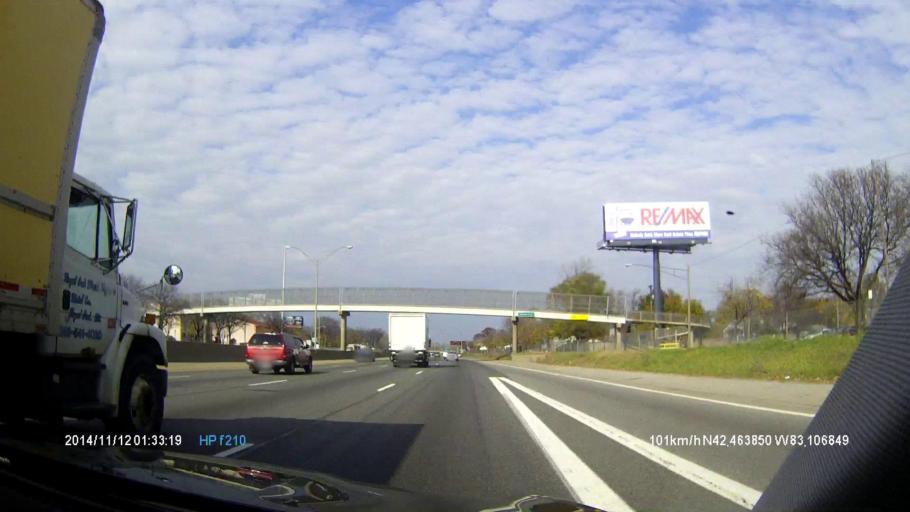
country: US
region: Michigan
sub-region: Oakland County
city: Hazel Park
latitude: 42.4639
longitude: -83.1069
